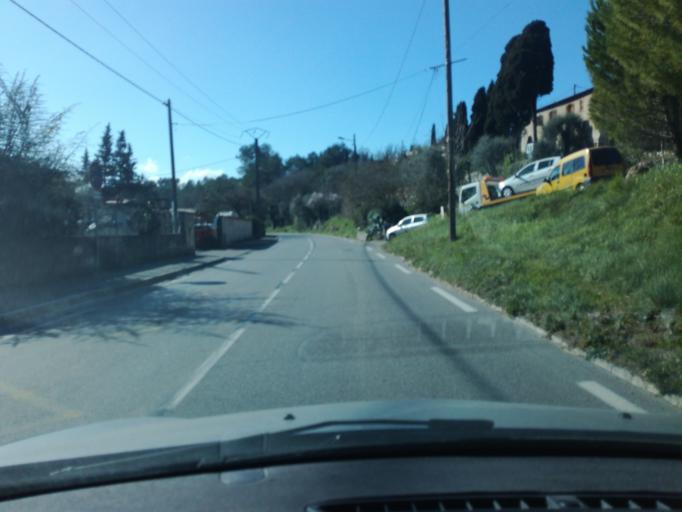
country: FR
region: Provence-Alpes-Cote d'Azur
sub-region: Departement des Alpes-Maritimes
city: Pegomas
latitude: 43.6286
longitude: 6.9286
